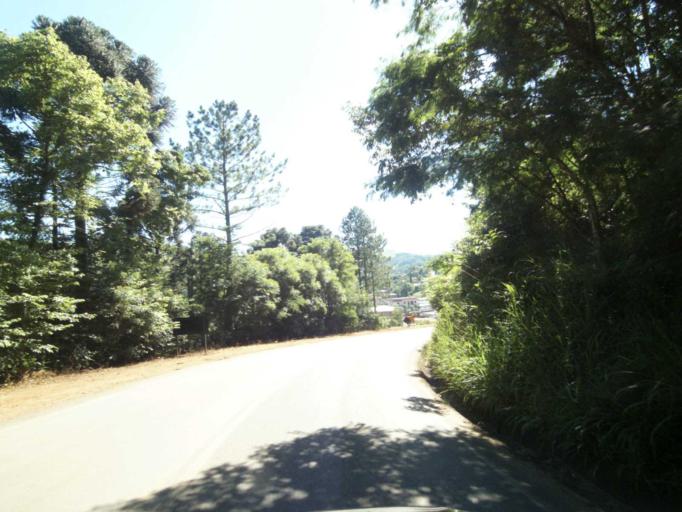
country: BR
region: Parana
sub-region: Francisco Beltrao
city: Francisco Beltrao
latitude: -26.1452
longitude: -53.3154
